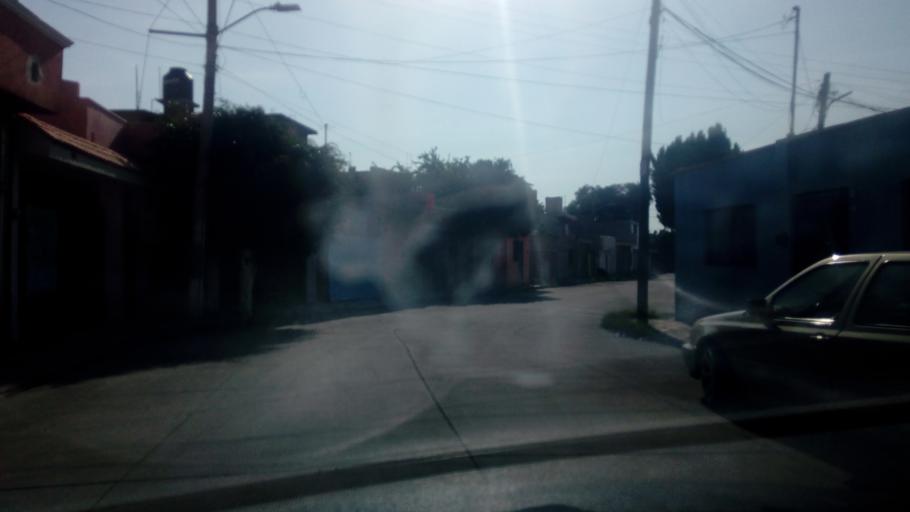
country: MX
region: Durango
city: Victoria de Durango
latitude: 24.0191
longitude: -104.6610
